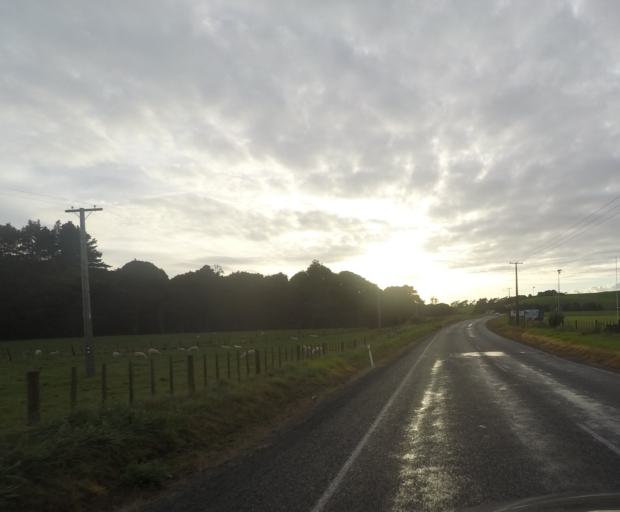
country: NZ
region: Auckland
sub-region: Auckland
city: Wellsford
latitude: -36.2203
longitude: 174.5790
